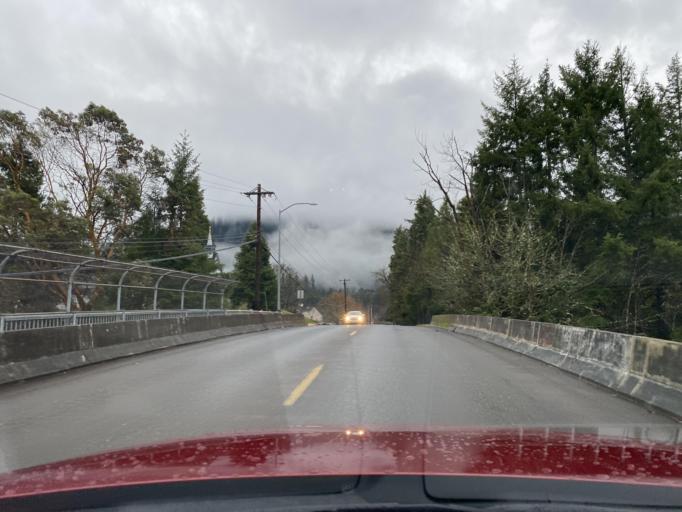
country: US
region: Oregon
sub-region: Lane County
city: Oakridge
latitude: 43.7468
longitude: -122.4671
